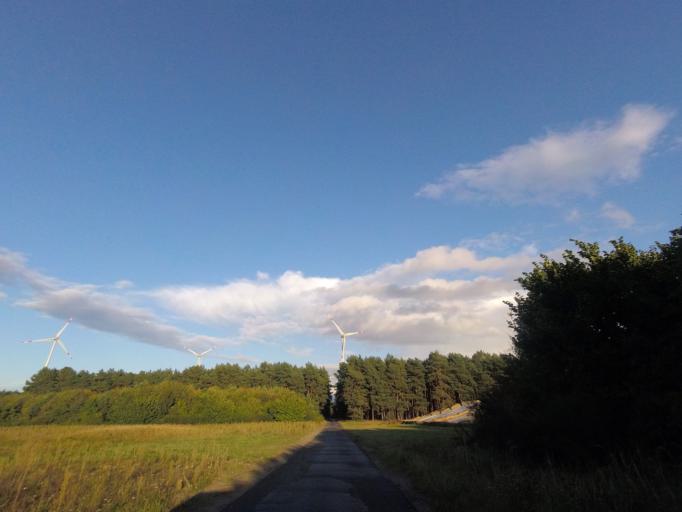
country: DE
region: Brandenburg
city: Treuenbrietzen
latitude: 52.0240
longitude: 12.8347
